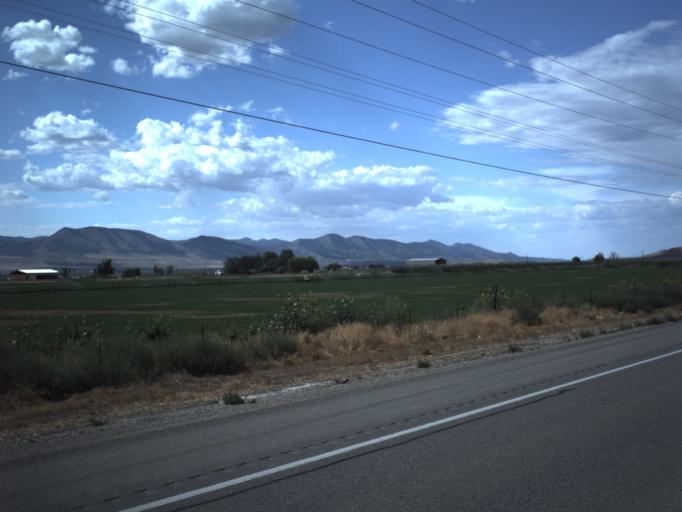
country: US
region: Utah
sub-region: Sanpete County
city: Centerfield
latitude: 39.0978
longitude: -111.8198
